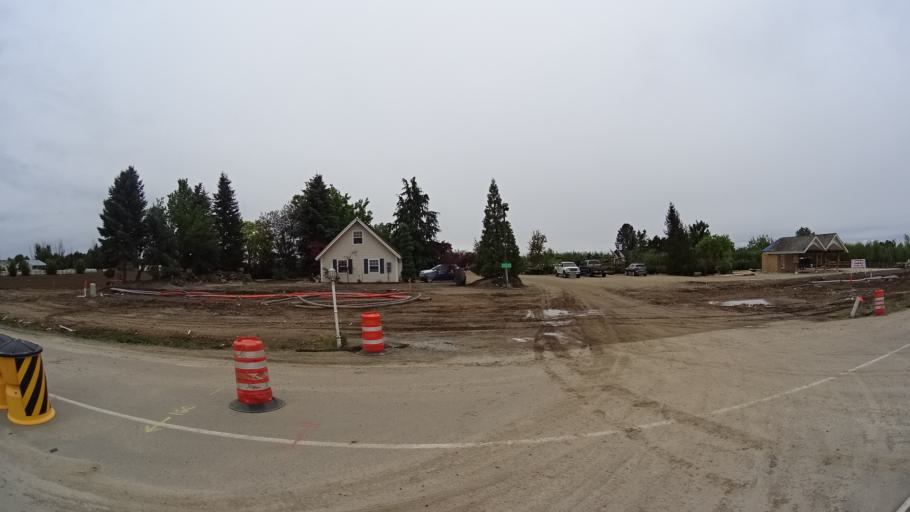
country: US
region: Idaho
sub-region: Ada County
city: Star
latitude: 43.6629
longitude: -116.4616
